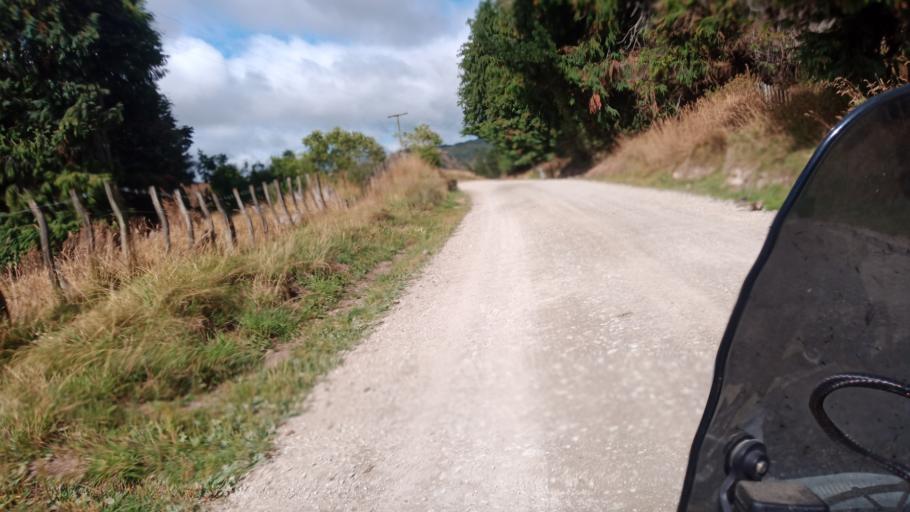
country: NZ
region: Hawke's Bay
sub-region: Wairoa District
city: Wairoa
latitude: -38.6081
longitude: 177.4482
